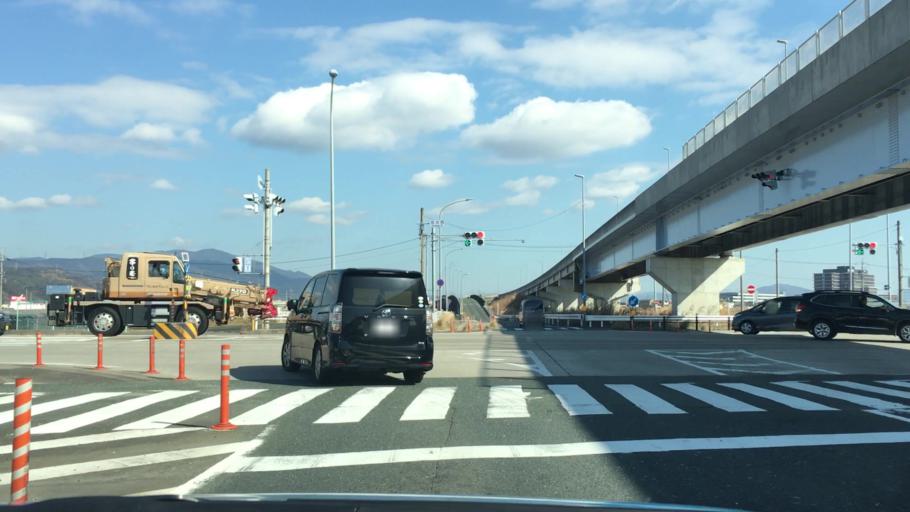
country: JP
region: Aichi
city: Kozakai-cho
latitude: 34.8264
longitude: 137.3397
